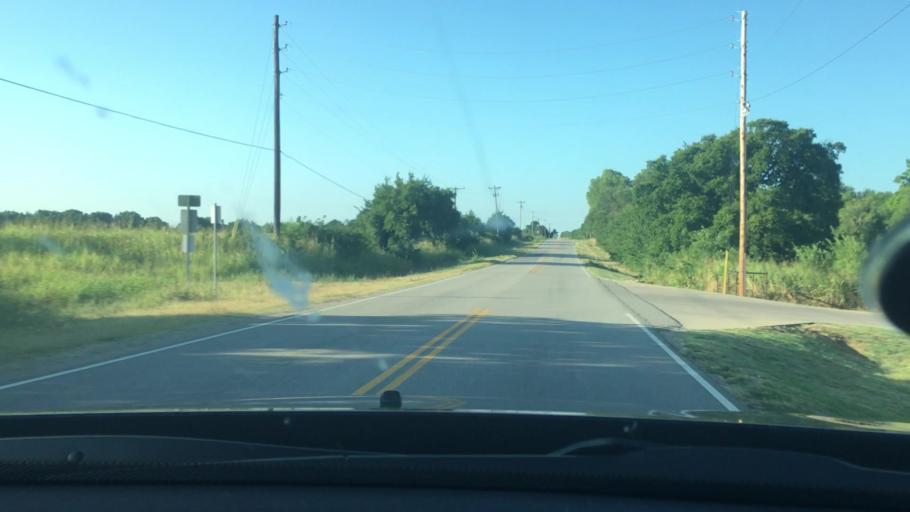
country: US
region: Oklahoma
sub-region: Murray County
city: Sulphur
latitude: 34.6191
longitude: -96.8447
